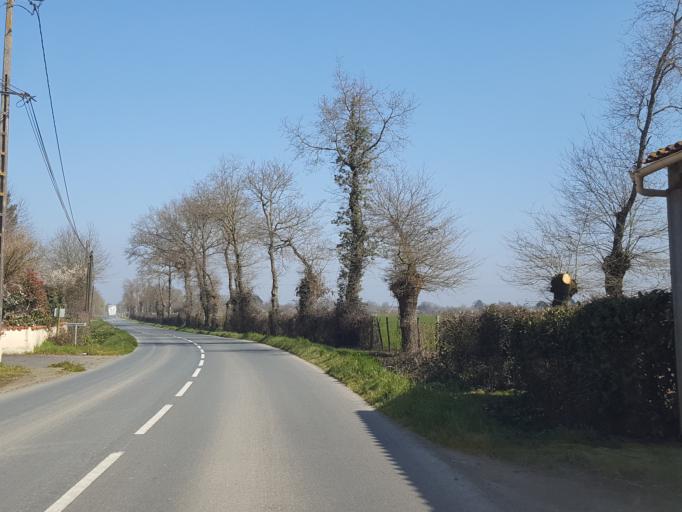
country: FR
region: Pays de la Loire
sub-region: Departement de la Vendee
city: La Chaize-le-Vicomte
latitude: 46.6610
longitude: -1.2977
